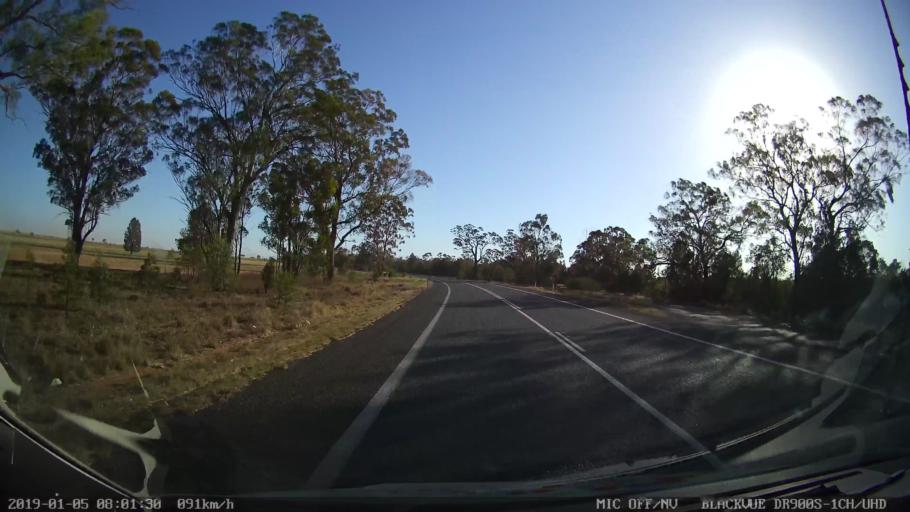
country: AU
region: New South Wales
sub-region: Gilgandra
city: Gilgandra
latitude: -31.6863
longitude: 148.7034
